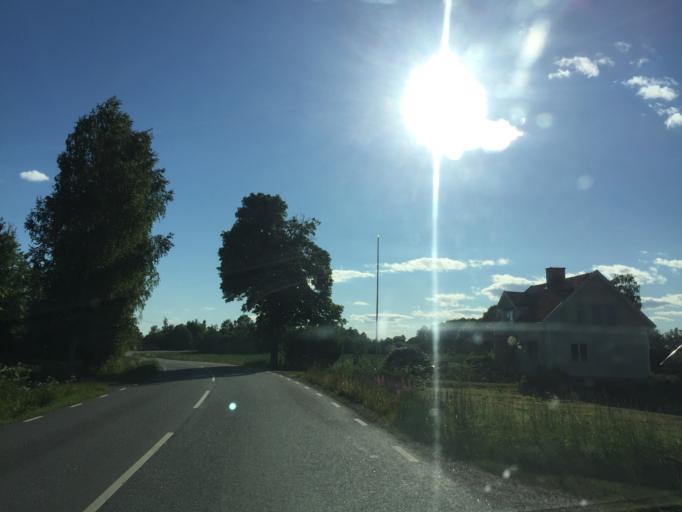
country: SE
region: OErebro
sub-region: Hallsbergs Kommun
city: Skollersta
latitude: 59.2016
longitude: 15.2779
